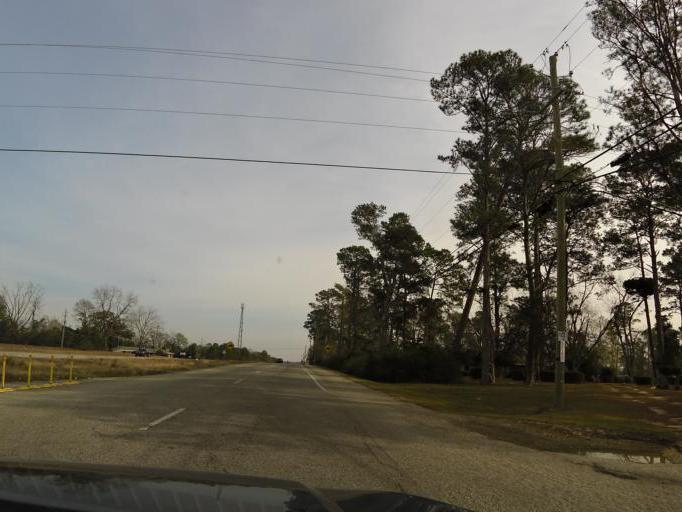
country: US
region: Alabama
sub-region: Houston County
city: Cowarts
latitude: 31.1945
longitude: -85.3246
